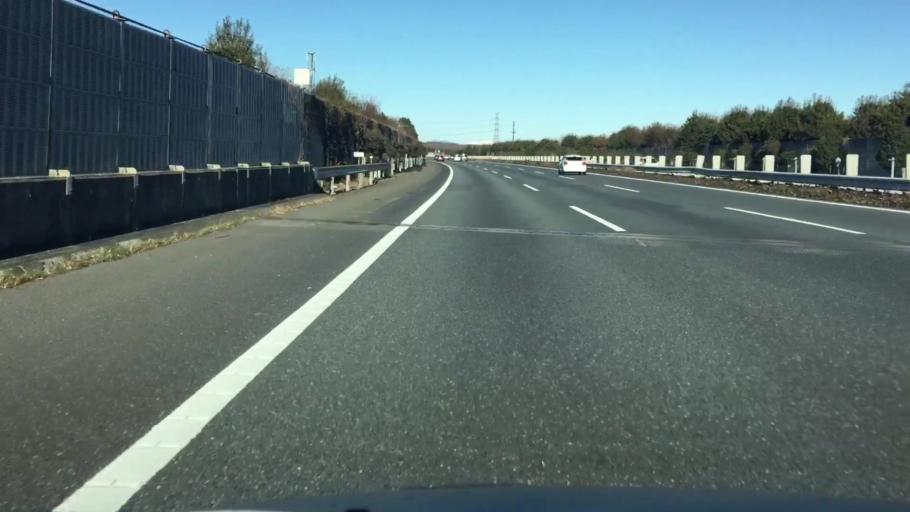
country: JP
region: Saitama
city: Honjo
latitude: 36.1936
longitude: 139.1881
